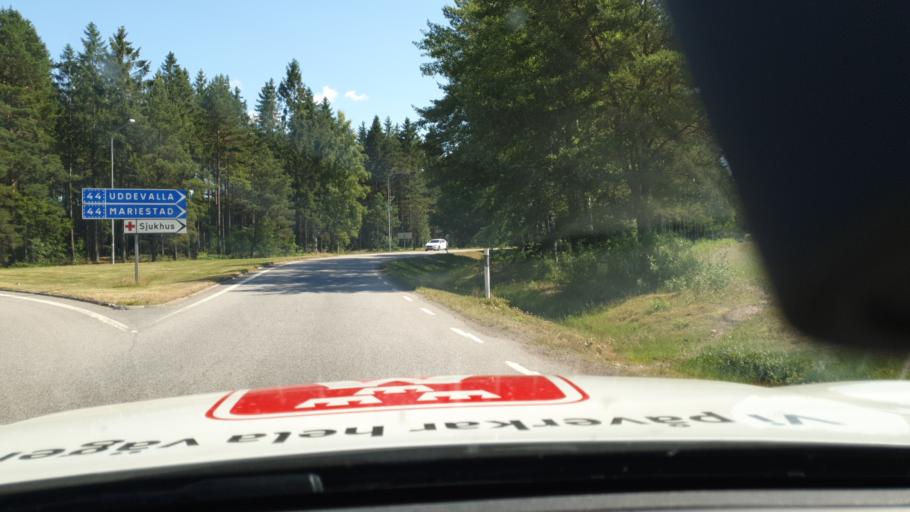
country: SE
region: Vaestra Goetaland
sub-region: Lidkopings Kommun
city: Lidkoping
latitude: 58.5186
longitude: 13.1133
